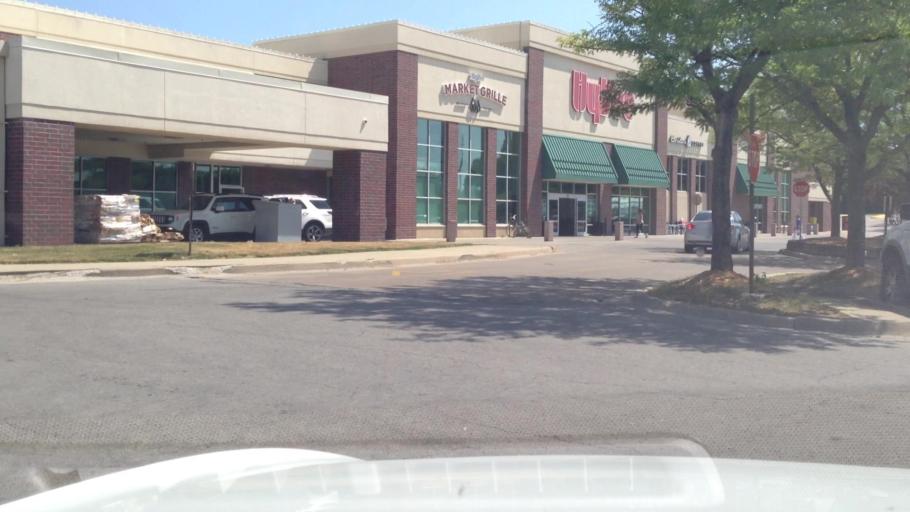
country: US
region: Kansas
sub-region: Douglas County
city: Lawrence
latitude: 38.9439
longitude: -95.2815
